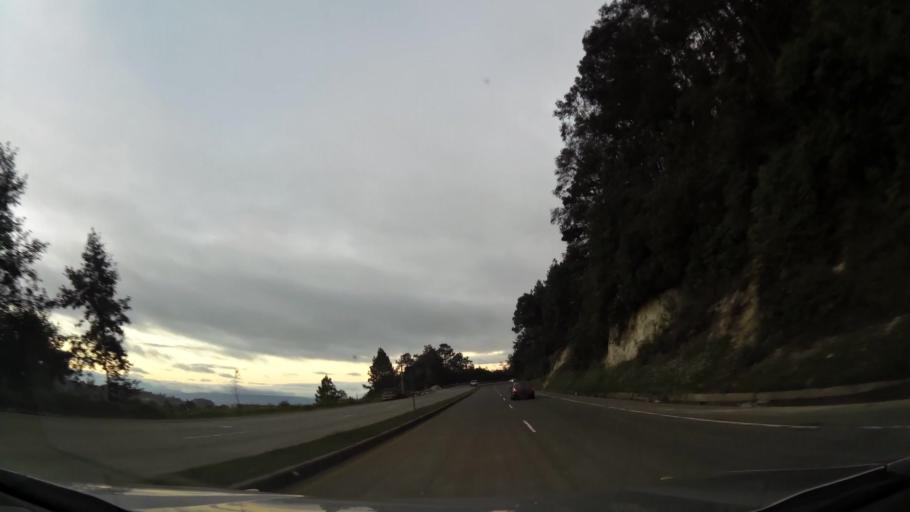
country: GT
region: Solola
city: Concepcion
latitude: 14.8334
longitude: -91.0767
